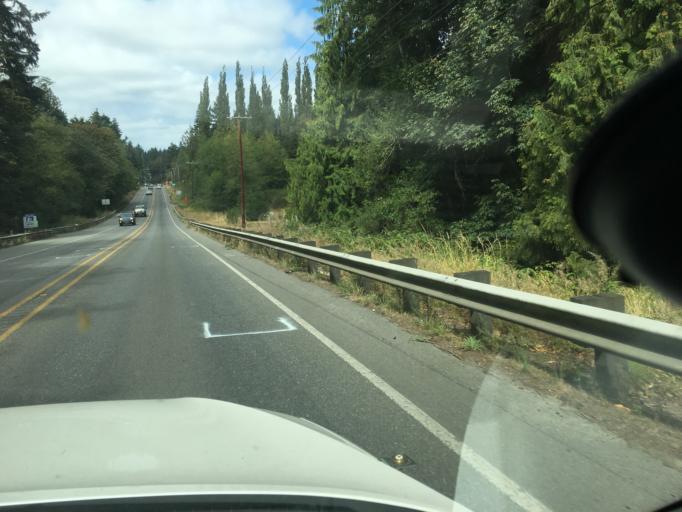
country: US
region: Washington
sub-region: Kitsap County
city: Kingston
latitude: 47.8060
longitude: -122.5117
